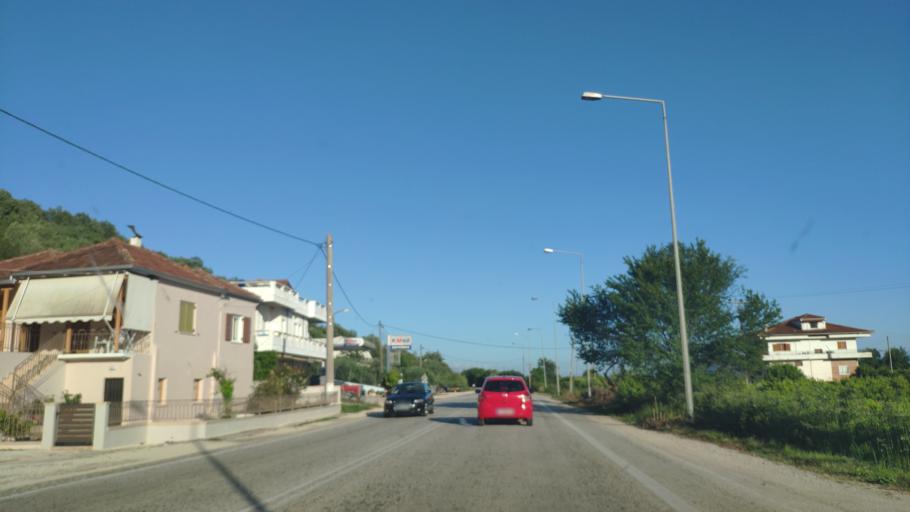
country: GR
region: Epirus
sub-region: Nomos Prevezis
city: Louros
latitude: 39.1766
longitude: 20.7898
